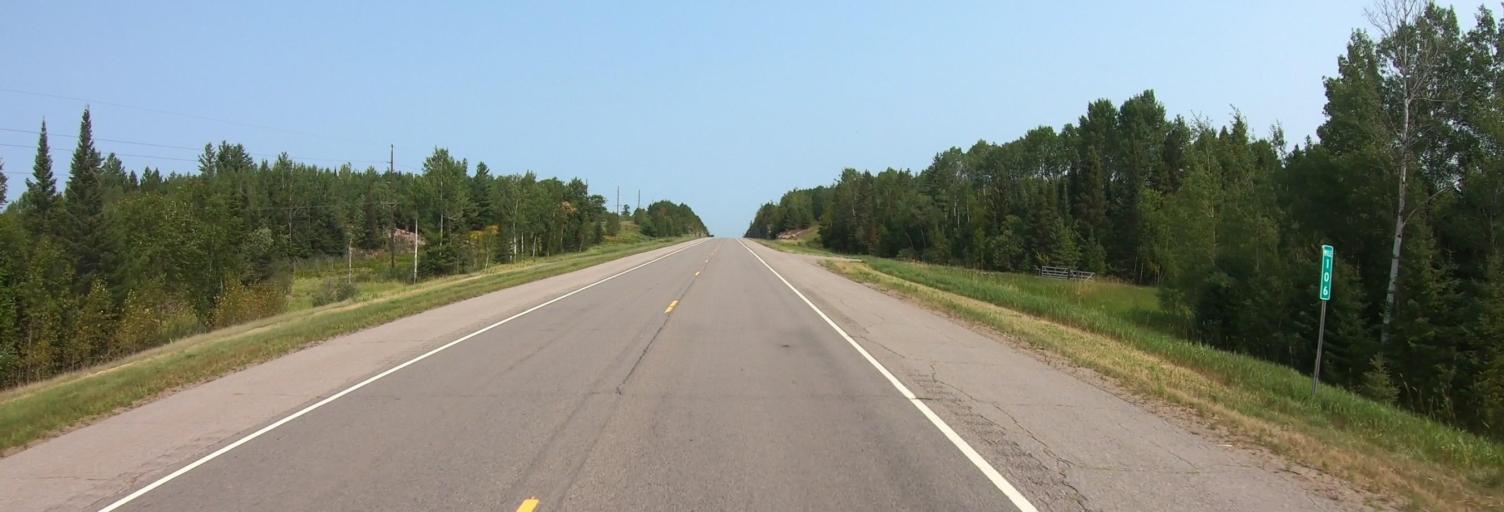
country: US
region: Minnesota
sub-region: Saint Louis County
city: Mountain Iron
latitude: 47.9977
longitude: -92.8308
